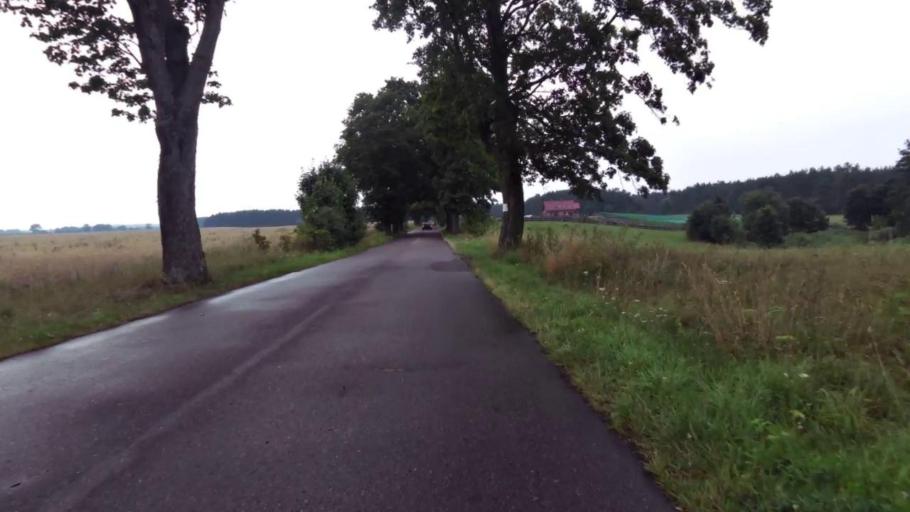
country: PL
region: West Pomeranian Voivodeship
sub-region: Powiat szczecinecki
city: Lubowo
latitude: 53.5906
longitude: 16.3748
